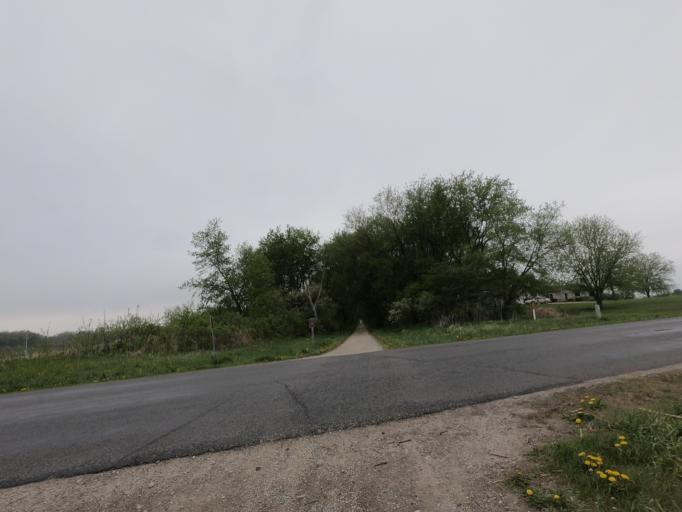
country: US
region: Wisconsin
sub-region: Jefferson County
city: Jefferson
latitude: 43.0425
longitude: -88.8466
